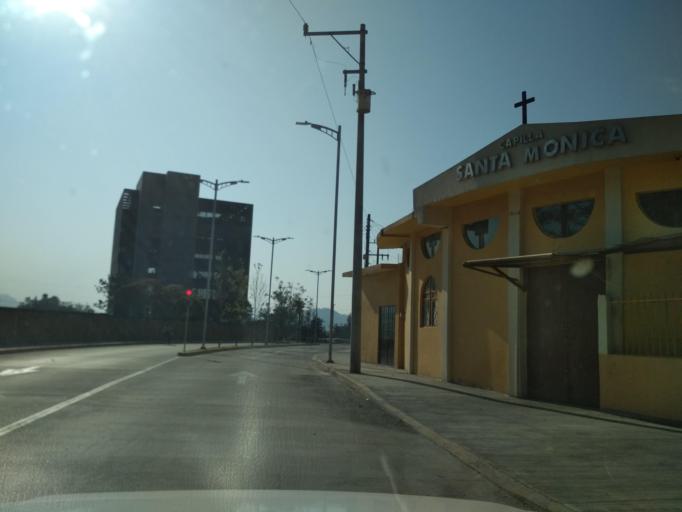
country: MX
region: Veracruz
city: Ixtac Zoquitlan
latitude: 18.8603
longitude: -97.0714
